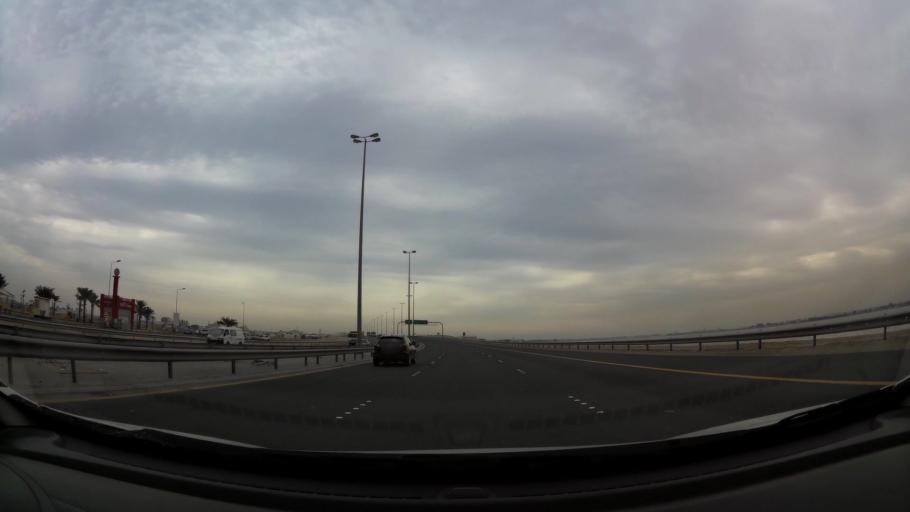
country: BH
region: Northern
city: Sitrah
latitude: 26.1783
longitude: 50.5929
